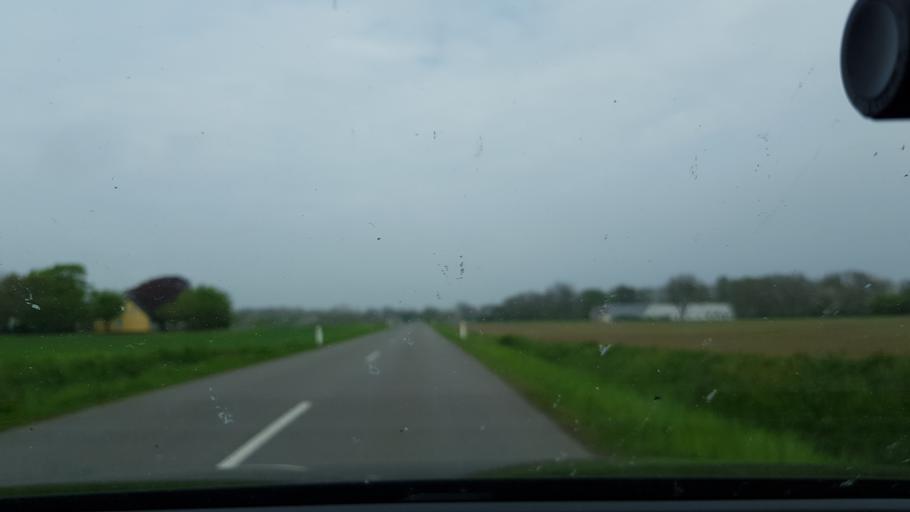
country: DK
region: Capital Region
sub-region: Bornholm Kommune
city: Nexo
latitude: 55.0209
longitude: 15.0968
